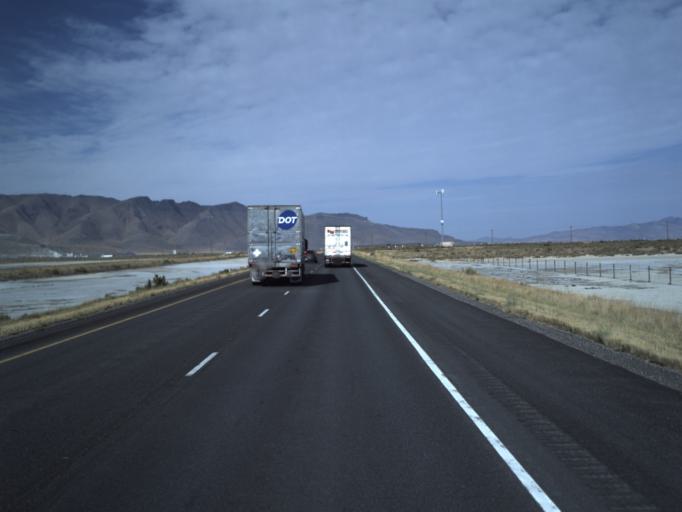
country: US
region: Utah
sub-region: Tooele County
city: Grantsville
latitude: 40.7044
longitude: -112.5071
